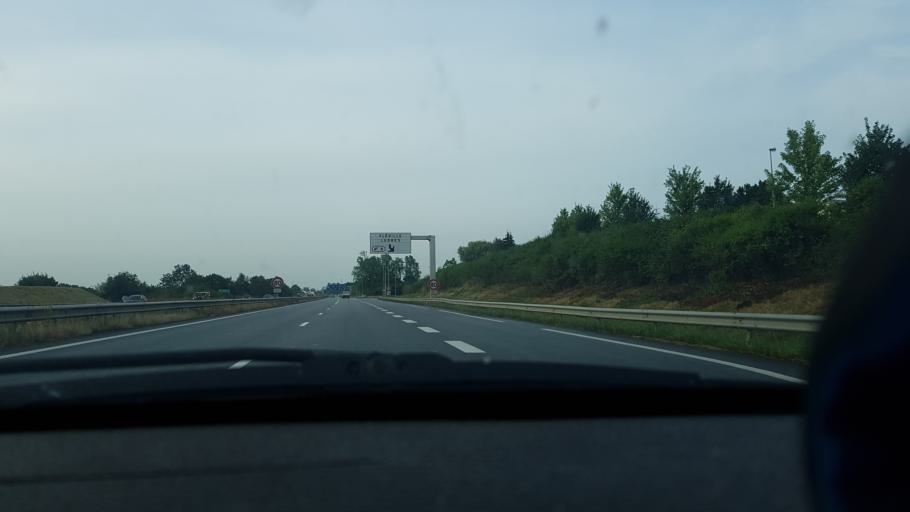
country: FR
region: Lorraine
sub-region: Departement de Meurthe-et-Moselle
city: Vandoeuvre-les-Nancy
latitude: 48.6387
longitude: 6.1812
